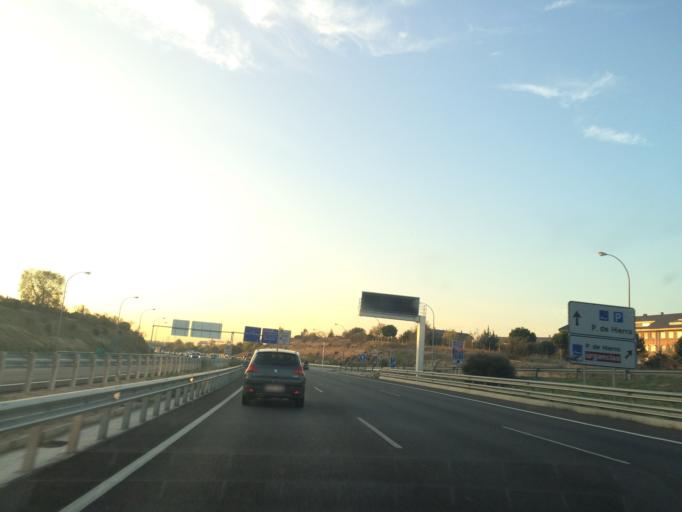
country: ES
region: Madrid
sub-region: Provincia de Madrid
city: Majadahonda
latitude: 40.4496
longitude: -3.8590
